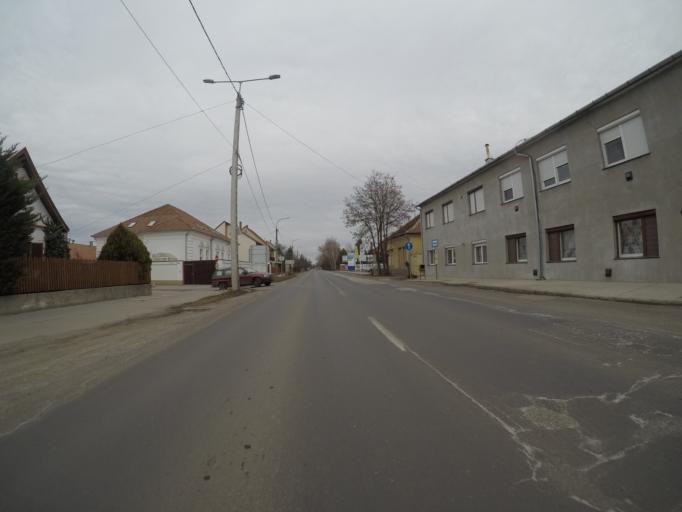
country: HU
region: Jasz-Nagykun-Szolnok
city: Jaszbereny
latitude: 47.5020
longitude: 19.9225
